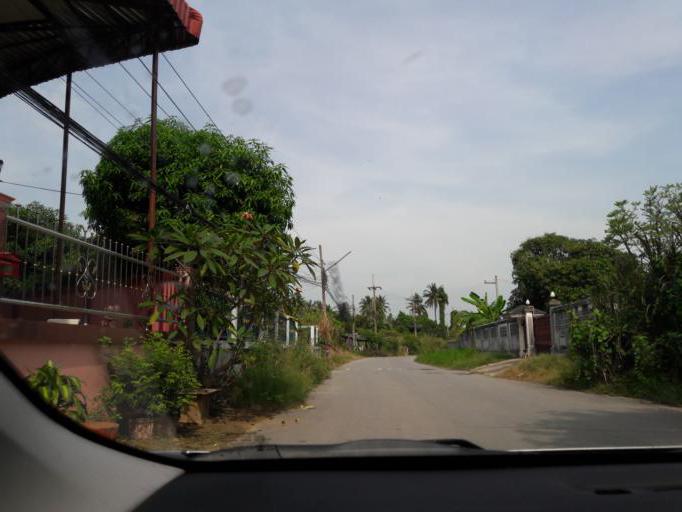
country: TH
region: Ang Thong
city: Ang Thong
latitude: 14.5841
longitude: 100.4626
